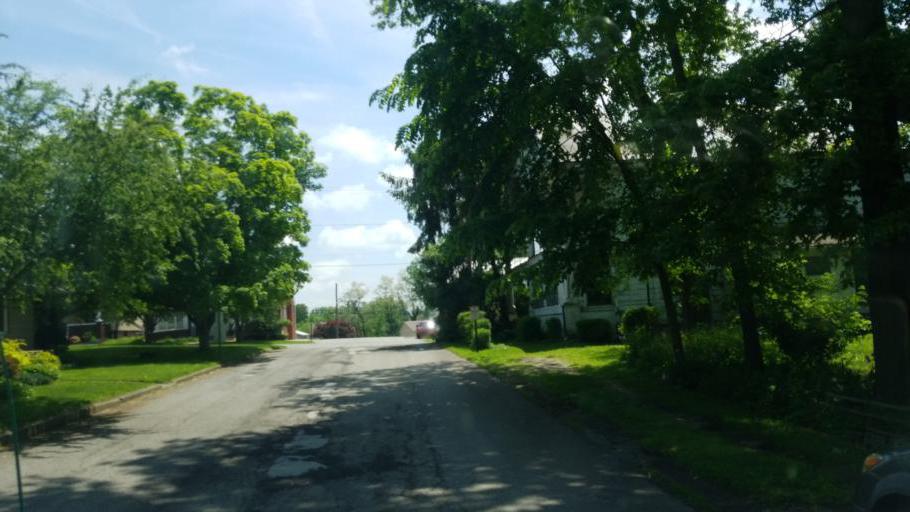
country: US
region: Ohio
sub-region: Ashland County
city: Ashland
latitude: 40.8038
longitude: -82.1970
